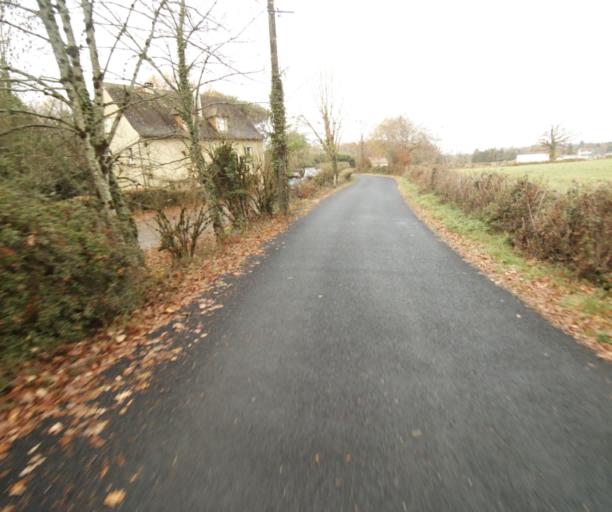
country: FR
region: Limousin
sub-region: Departement de la Correze
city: Saint-Mexant
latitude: 45.2682
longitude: 1.6355
